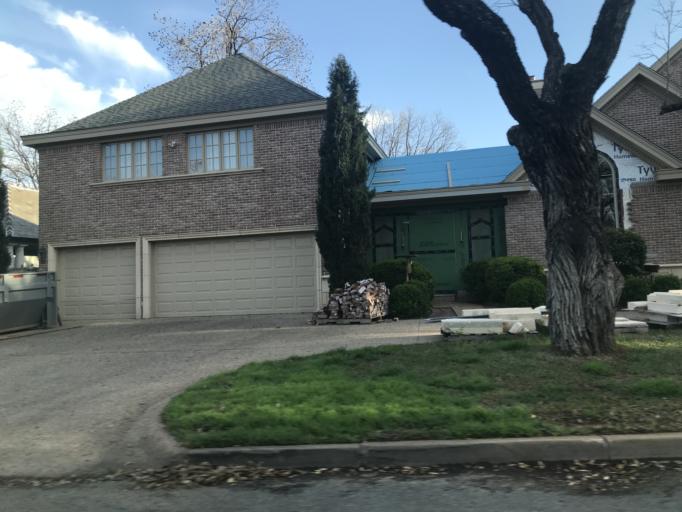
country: US
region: Texas
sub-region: Taylor County
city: Abilene
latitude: 32.4367
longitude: -99.7709
